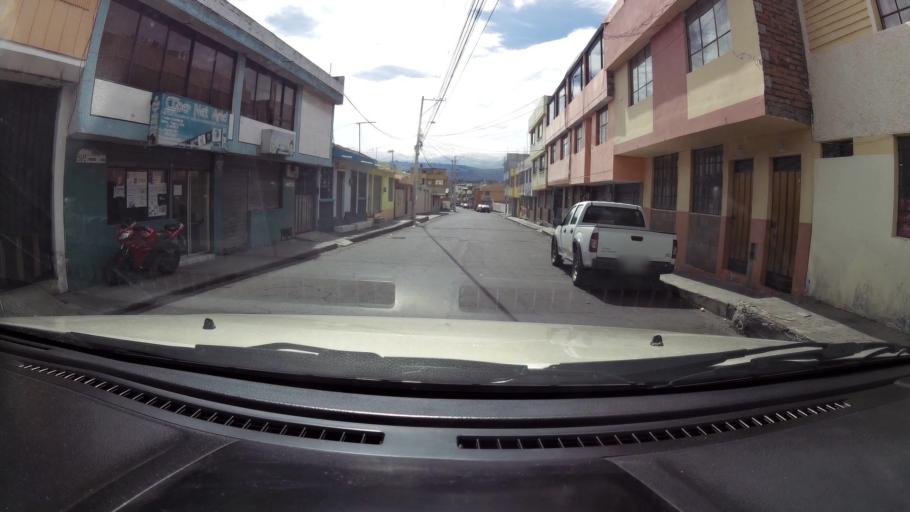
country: EC
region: Cotopaxi
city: Latacunga
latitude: -0.9292
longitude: -78.6218
